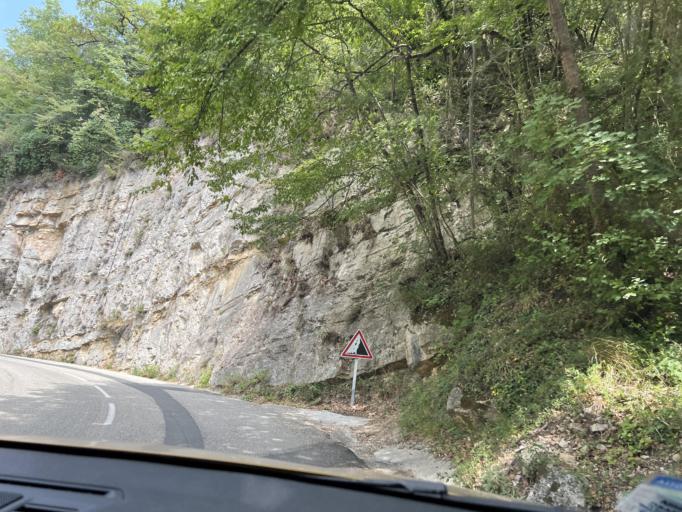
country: FR
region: Provence-Alpes-Cote d'Azur
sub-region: Departement des Alpes-Maritimes
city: Le Rouret
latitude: 43.7270
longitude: 6.9974
